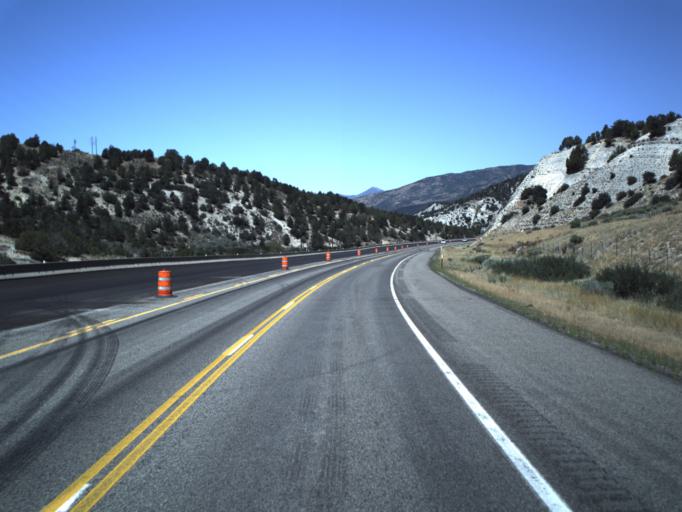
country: US
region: Utah
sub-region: Utah County
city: Mapleton
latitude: 39.9555
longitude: -111.2985
